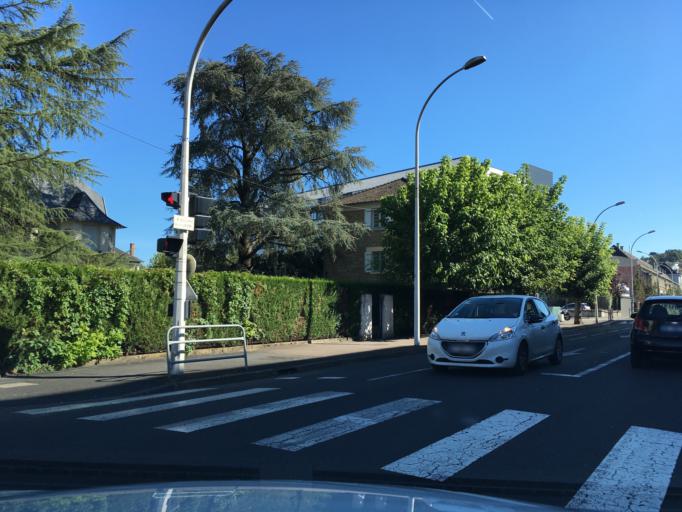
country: FR
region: Limousin
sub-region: Departement de la Correze
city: Brive-la-Gaillarde
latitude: 45.1606
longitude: 1.5232
